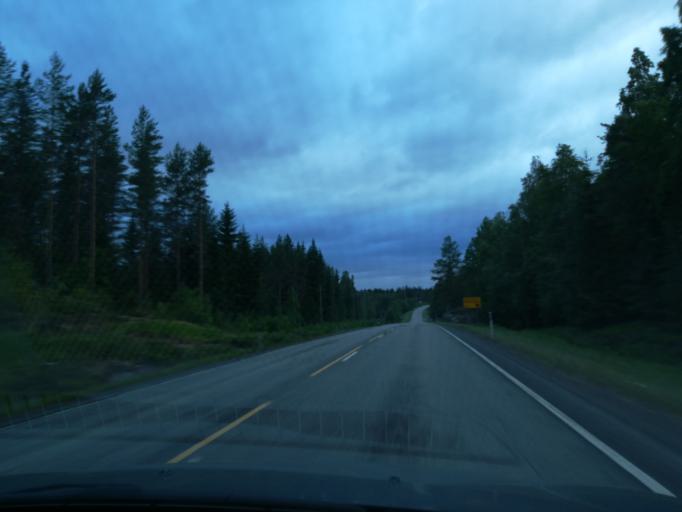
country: FI
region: Southern Savonia
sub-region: Mikkeli
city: Ristiina
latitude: 61.4554
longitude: 27.2618
